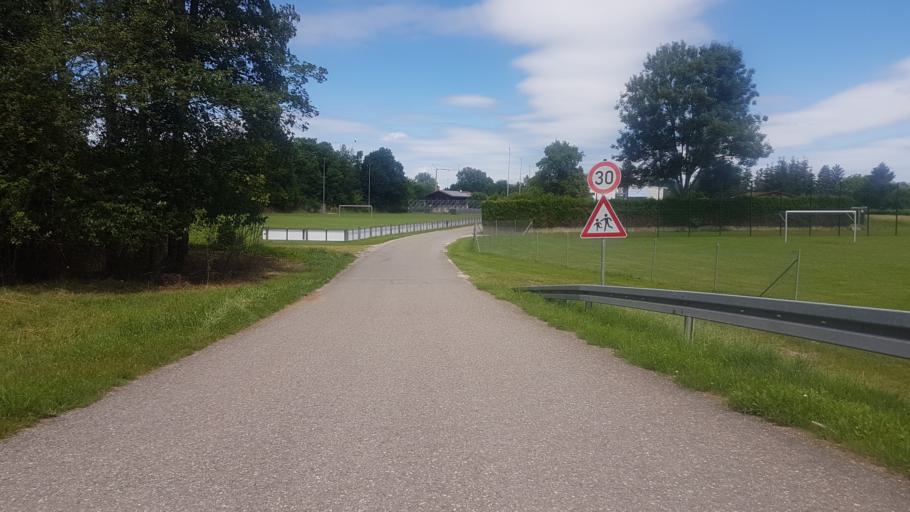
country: DE
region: Bavaria
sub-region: Swabia
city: Hochstadt an der Donau
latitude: 48.5904
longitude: 10.5396
